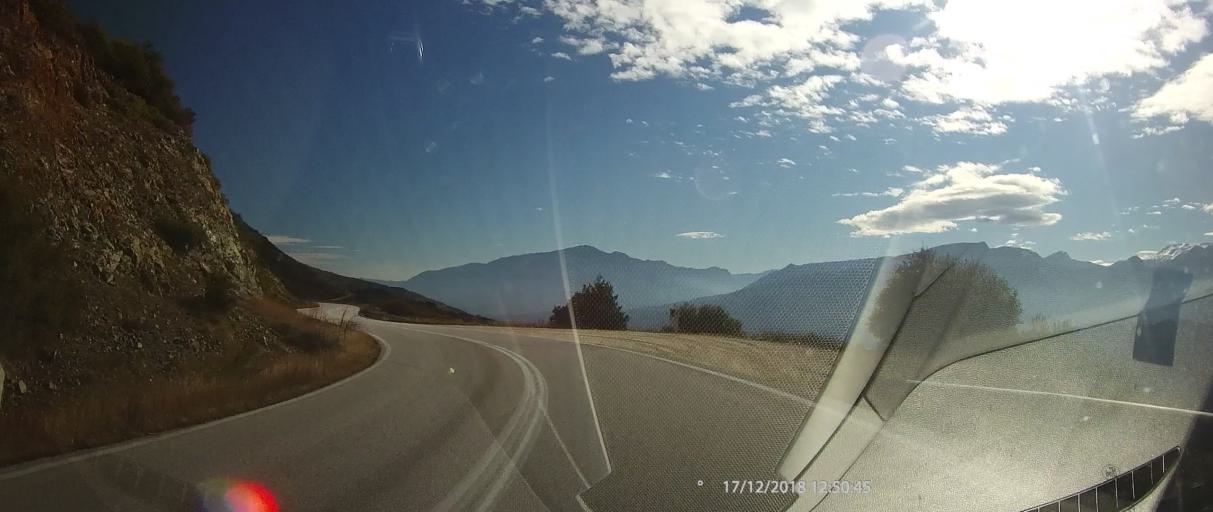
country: GR
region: Thessaly
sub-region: Trikala
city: Kastraki
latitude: 39.7719
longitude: 21.4563
